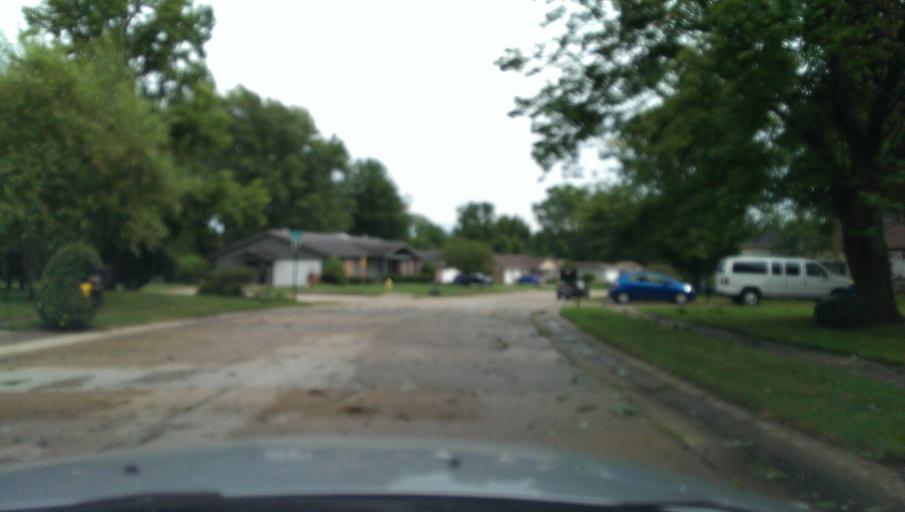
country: US
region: Indiana
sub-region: Hamilton County
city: Carmel
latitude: 39.9950
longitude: -86.1328
